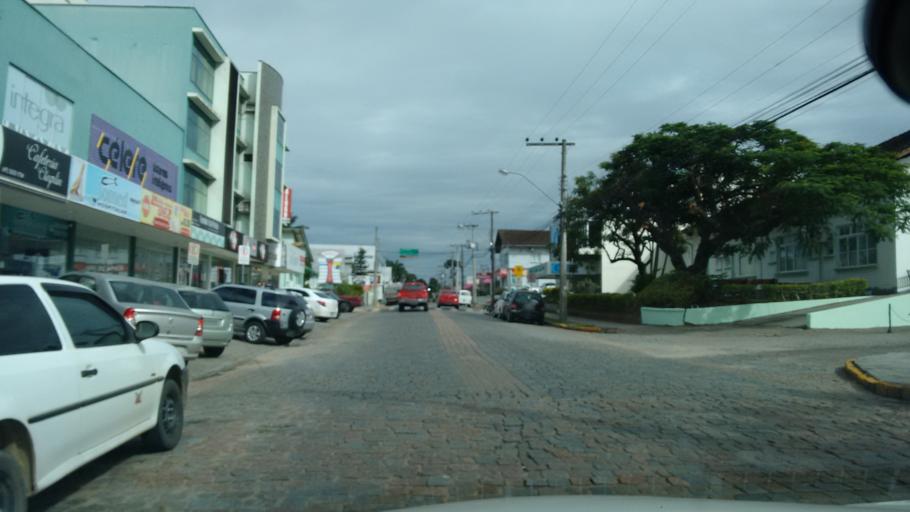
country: BR
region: Santa Catarina
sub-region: Timbo
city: Timbo
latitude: -26.8261
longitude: -49.2723
